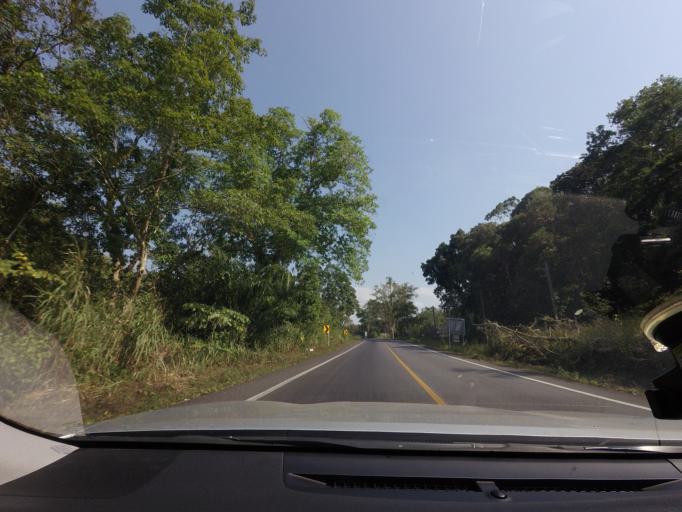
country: TH
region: Krabi
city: Plai Phraya
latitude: 8.5576
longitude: 98.7805
